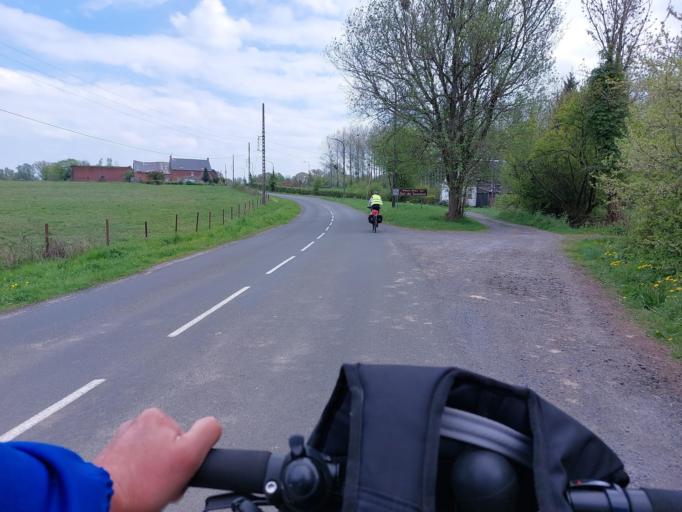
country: FR
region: Nord-Pas-de-Calais
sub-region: Departement du Nord
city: La Longueville
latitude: 50.2716
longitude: 3.8879
